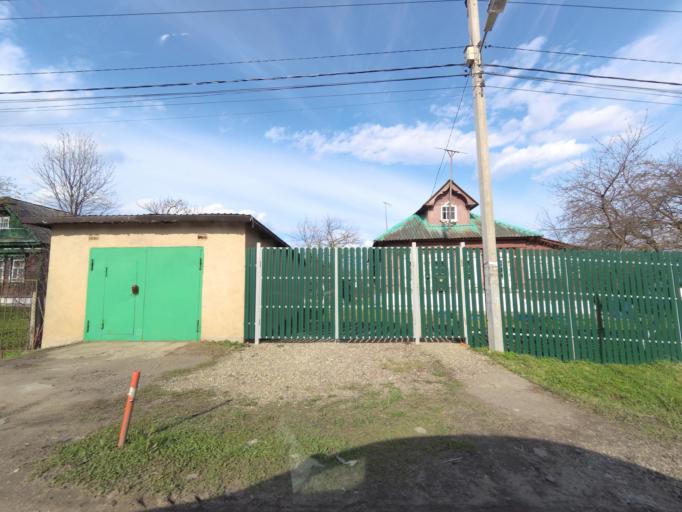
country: RU
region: Moskovskaya
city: Lobnya
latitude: 56.0231
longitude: 37.4341
